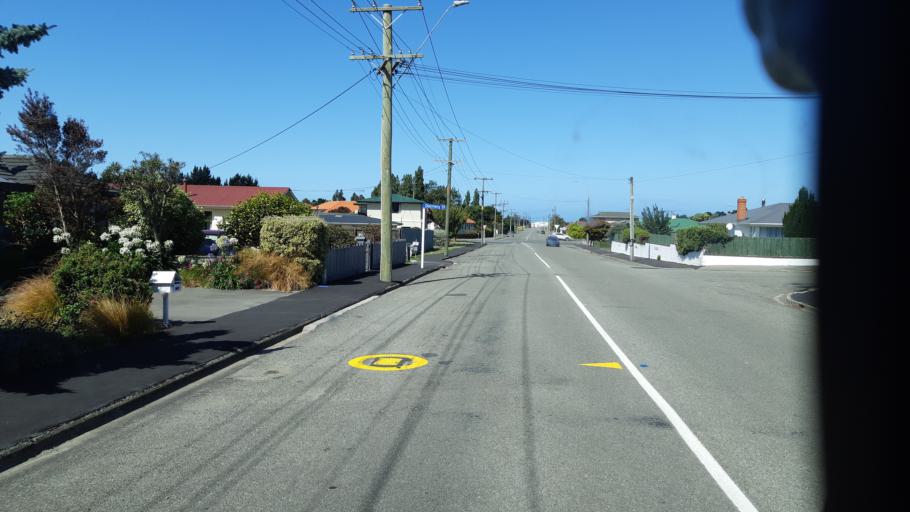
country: NZ
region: Otago
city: Oamaru
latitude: -45.0683
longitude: 170.9917
